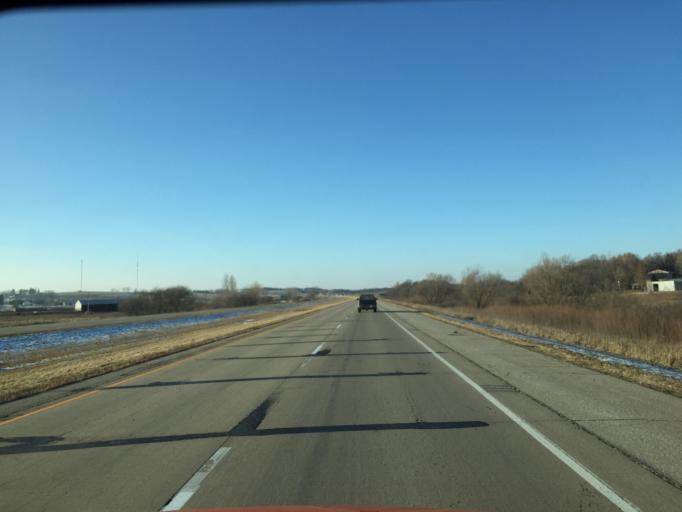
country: US
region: Minnesota
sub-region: Olmsted County
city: Rochester
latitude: 43.9663
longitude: -92.3940
